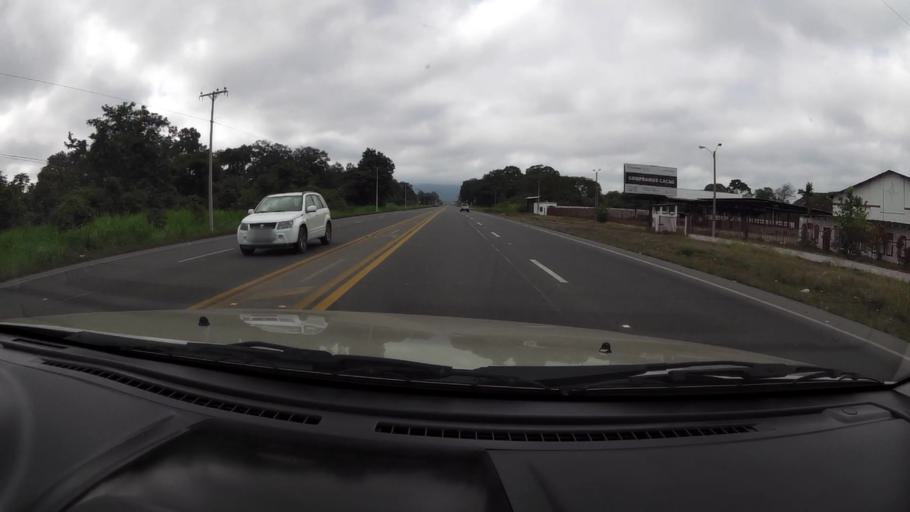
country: EC
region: Guayas
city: Naranjal
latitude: -2.6487
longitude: -79.6172
